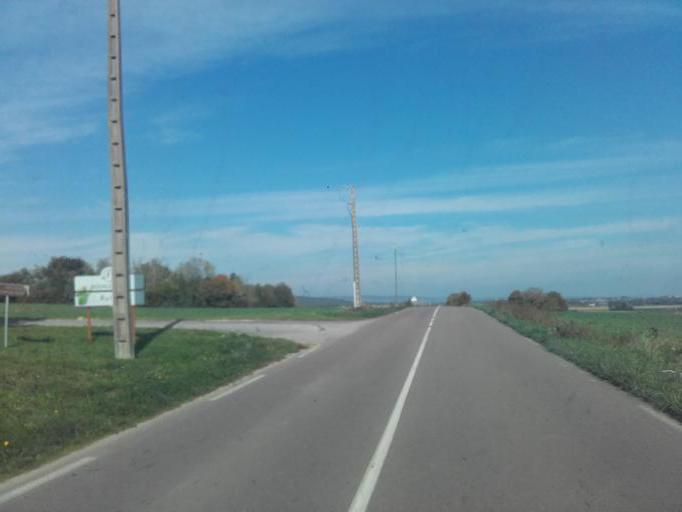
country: FR
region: Bourgogne
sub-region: Departement de Saone-et-Loire
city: Fontaines
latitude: 46.8568
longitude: 4.7525
